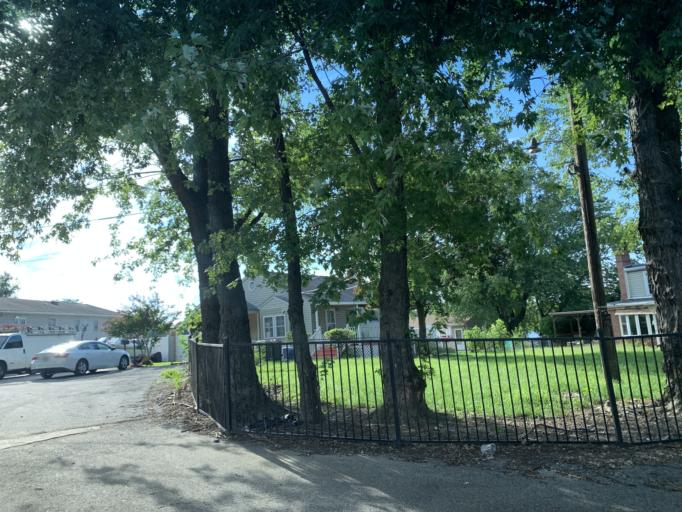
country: US
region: Maryland
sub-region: Baltimore County
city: Essex
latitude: 39.3078
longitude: -76.4873
